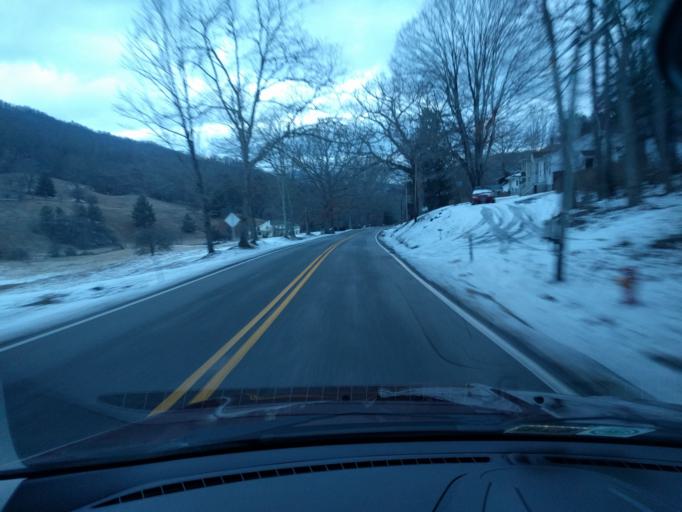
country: US
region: Virginia
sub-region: Alleghany County
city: Clifton Forge
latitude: 37.9314
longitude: -79.8825
